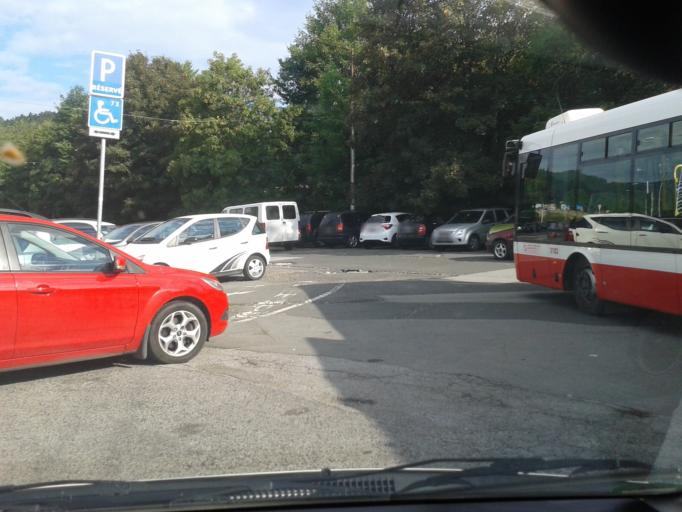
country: SK
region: Banskobystricky
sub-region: Okres Banska Bystrica
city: Banska Bystrica
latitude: 48.7446
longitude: 19.1185
